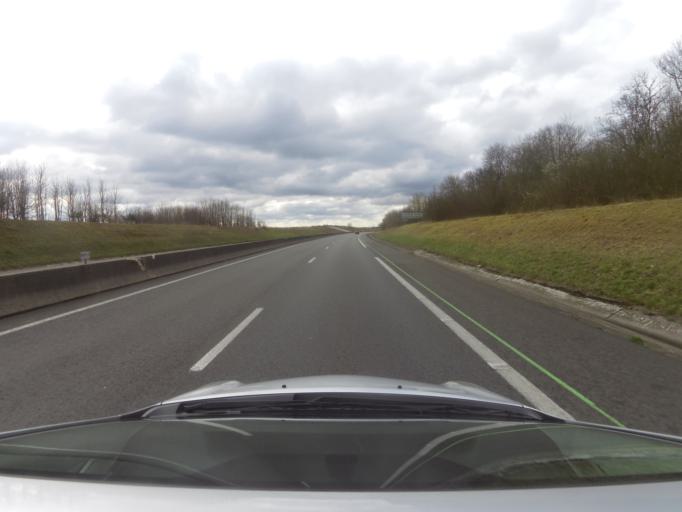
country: FR
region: Nord-Pas-de-Calais
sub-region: Departement du Pas-de-Calais
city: Etaples
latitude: 50.5266
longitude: 1.6858
